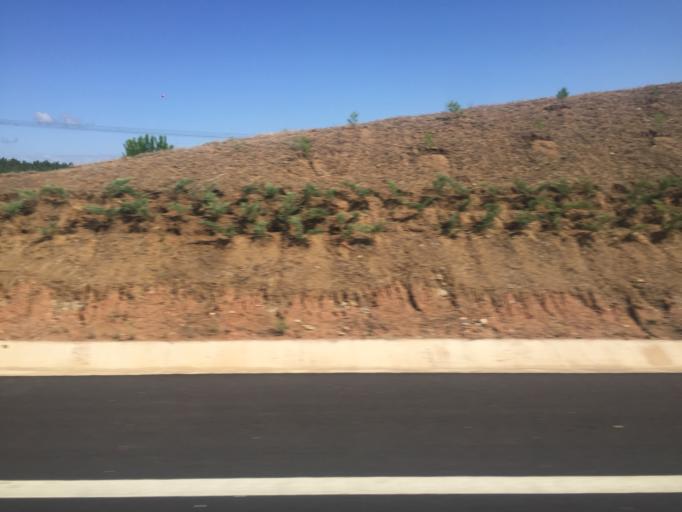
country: TR
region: Bursa
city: Mahmudiye
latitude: 40.2741
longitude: 28.5587
